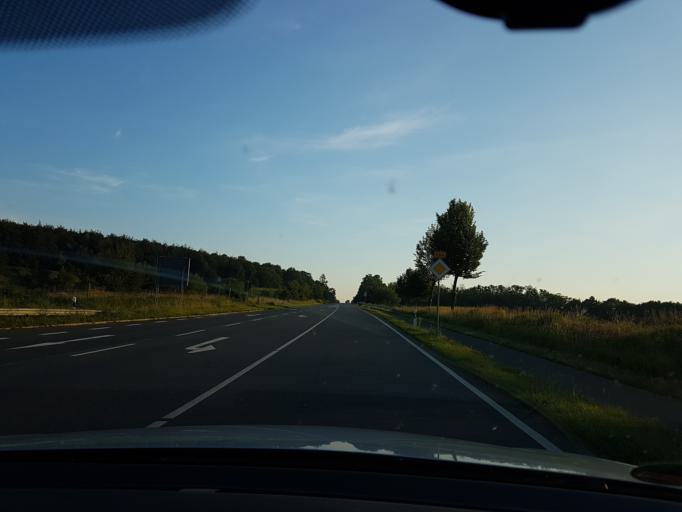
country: DE
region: Lower Saxony
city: Schoningen
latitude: 52.1759
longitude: 10.9761
